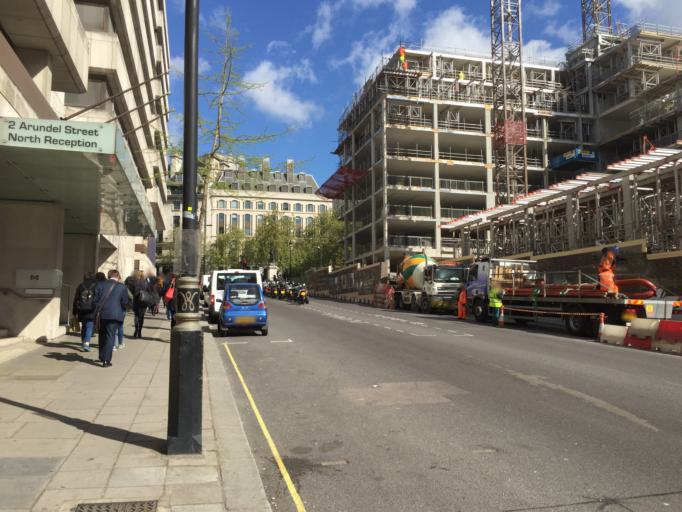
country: GB
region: England
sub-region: Greater London
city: London
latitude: 51.5120
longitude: -0.1141
